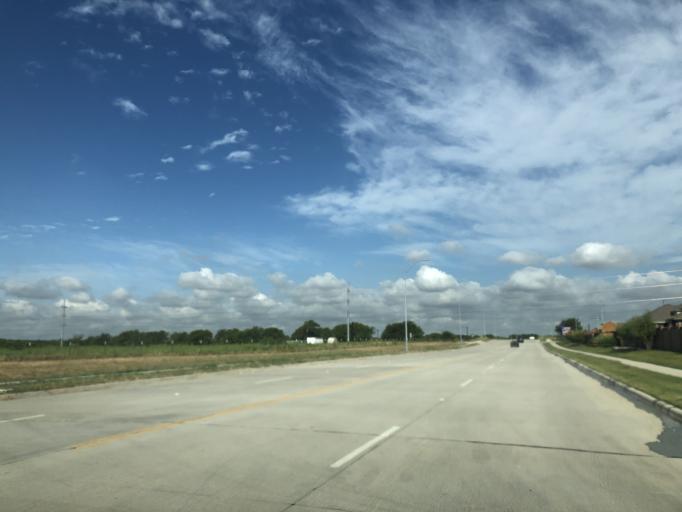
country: US
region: Texas
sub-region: Tarrant County
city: Haslet
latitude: 33.0188
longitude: -97.3095
